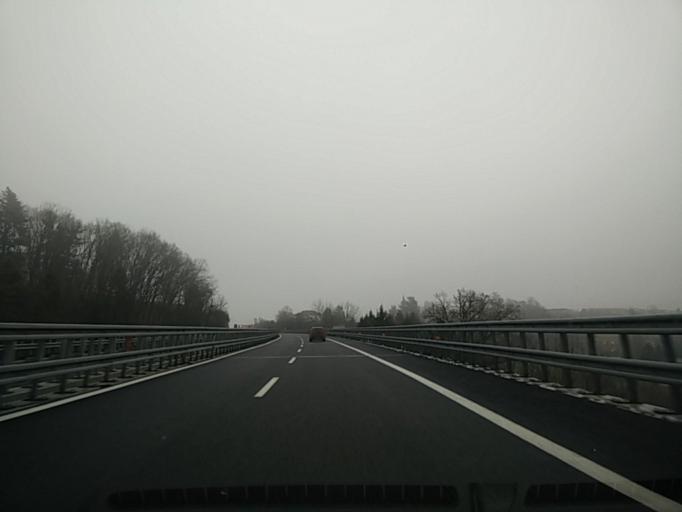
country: IT
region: Piedmont
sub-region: Provincia di Asti
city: Asti
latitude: 44.9160
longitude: 8.2101
